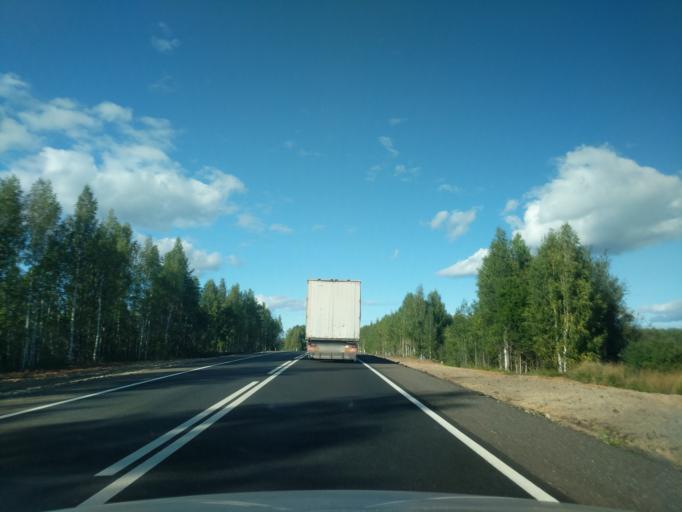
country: RU
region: Kostroma
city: Makar'yev
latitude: 57.9885
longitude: 43.9649
